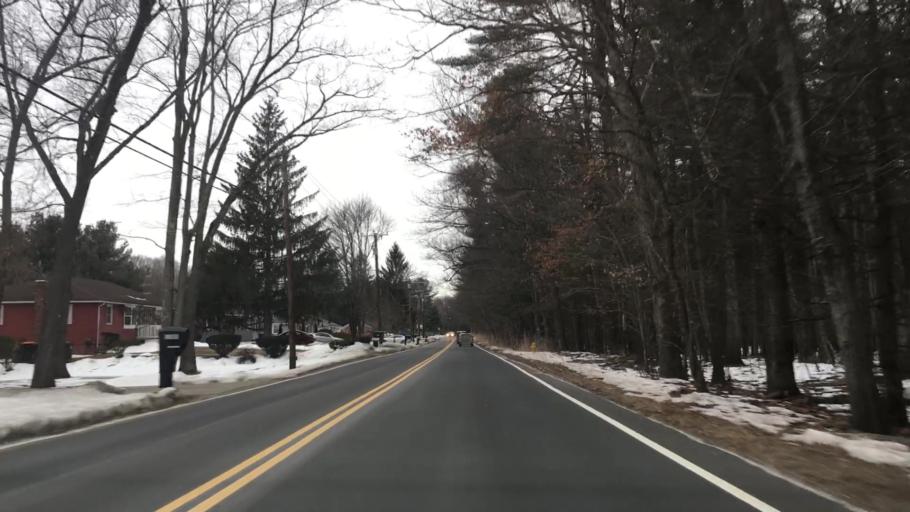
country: US
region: Massachusetts
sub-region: Hampden County
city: Westfield
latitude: 42.1016
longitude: -72.6893
